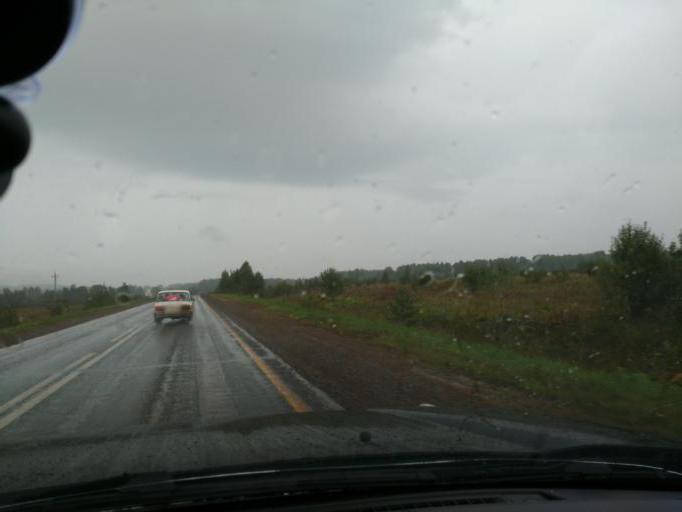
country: RU
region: Perm
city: Osa
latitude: 57.1417
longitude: 55.5283
